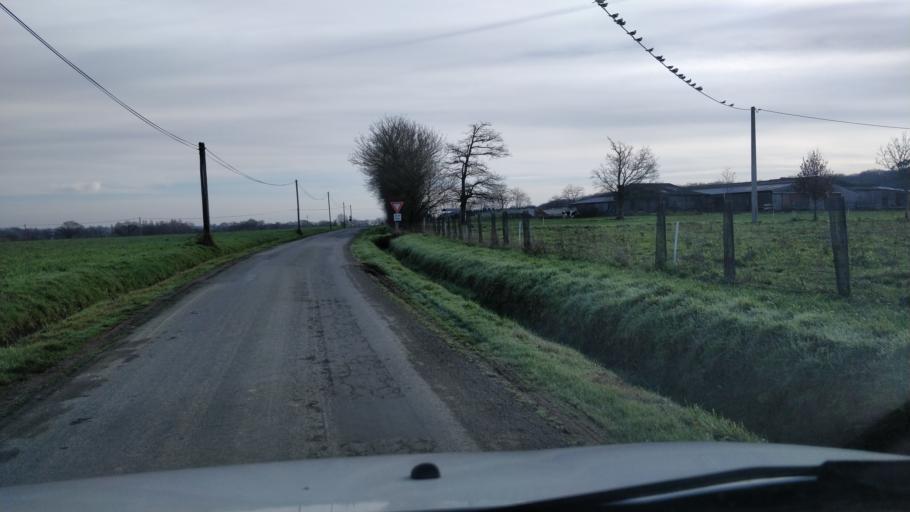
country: FR
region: Brittany
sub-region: Departement d'Ille-et-Vilaine
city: Argentre-du-Plessis
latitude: 48.0286
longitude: -1.1709
